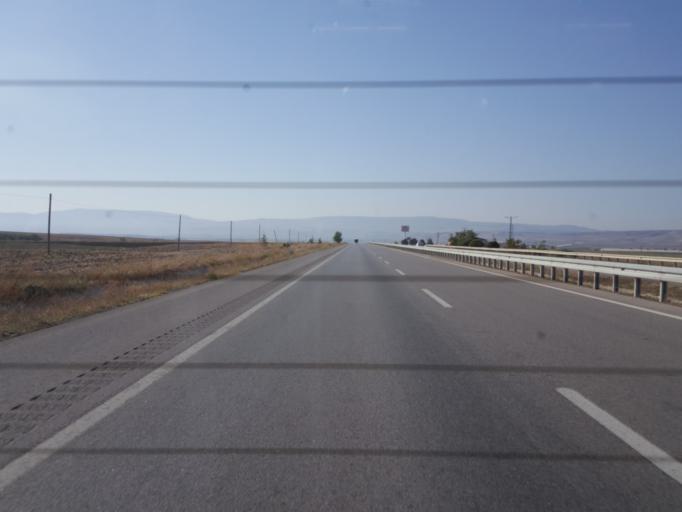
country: TR
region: Amasya
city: Merzifon
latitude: 40.8328
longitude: 35.4598
